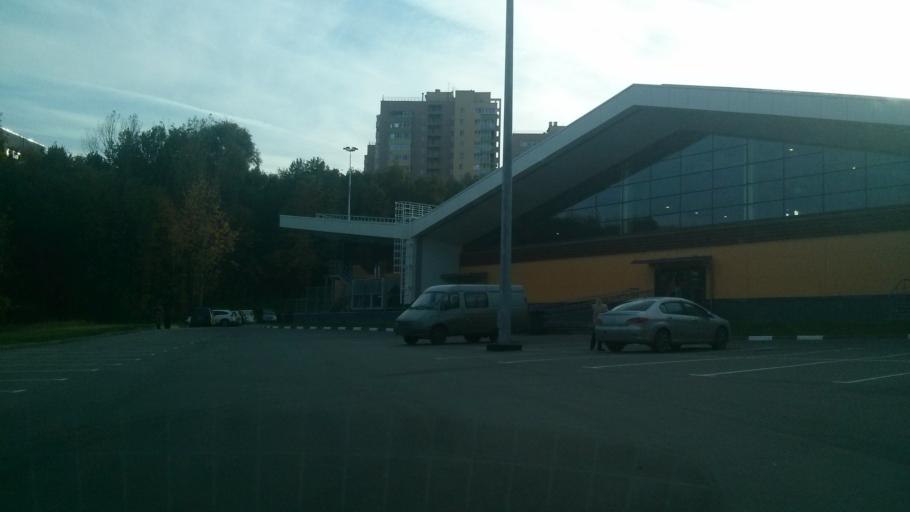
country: RU
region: Nizjnij Novgorod
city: Nizhniy Novgorod
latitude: 56.2963
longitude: 44.0476
